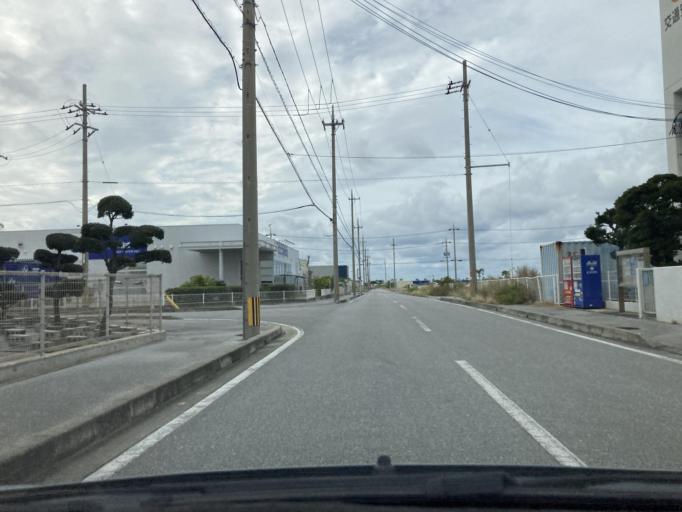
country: JP
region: Okinawa
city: Itoman
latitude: 26.1553
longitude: 127.6544
